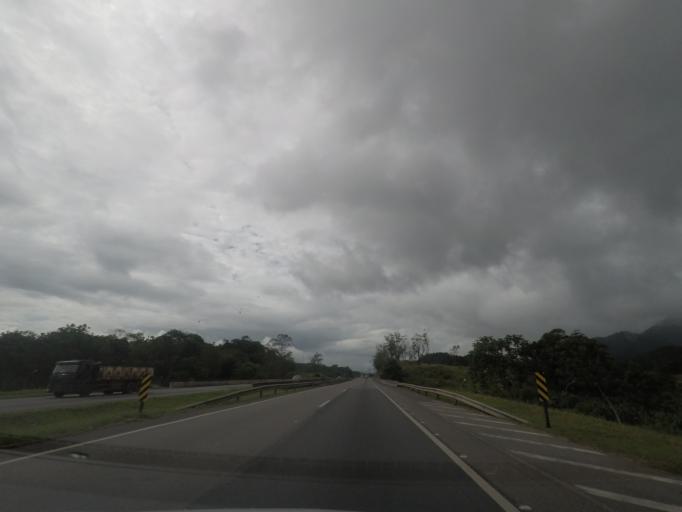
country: BR
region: Sao Paulo
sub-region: Miracatu
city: Miracatu
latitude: -24.2712
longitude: -47.4024
